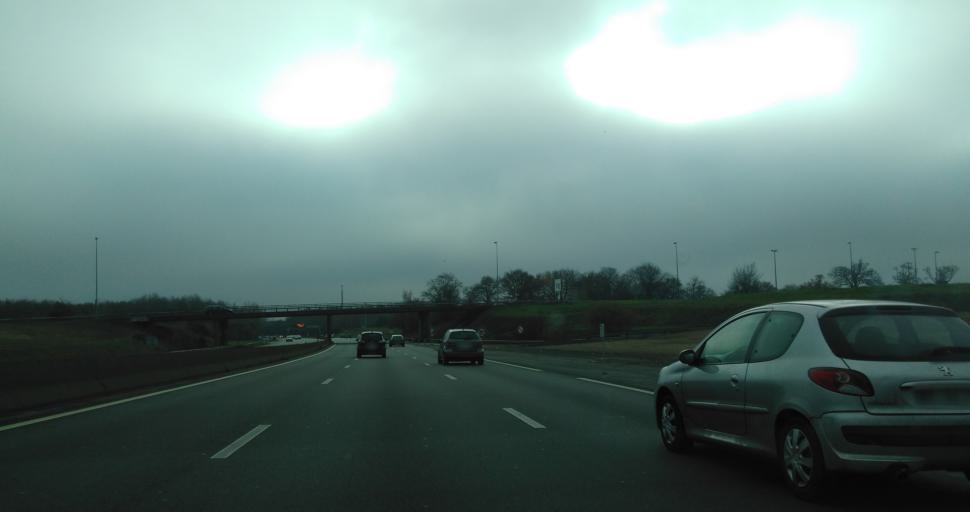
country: FR
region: Brittany
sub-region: Departement d'Ille-et-Vilaine
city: Saint-Jacques-de-la-Lande
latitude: 48.1051
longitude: -1.7156
